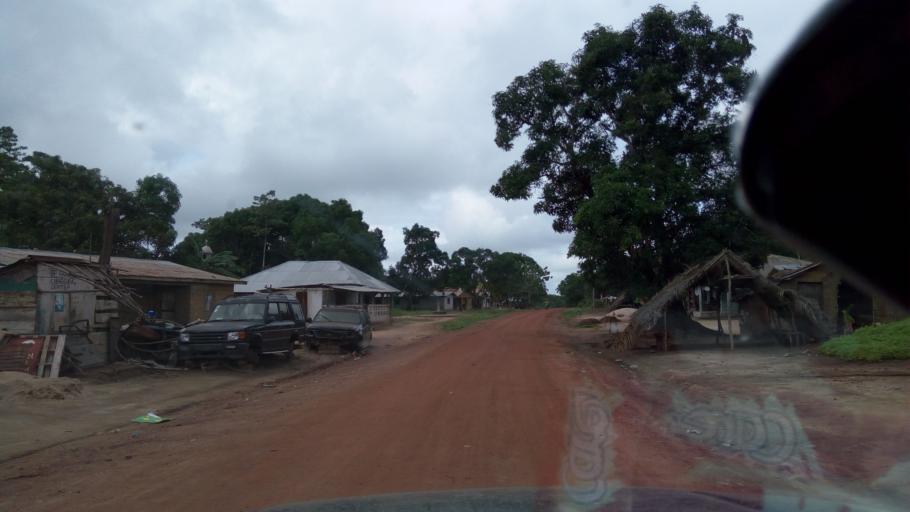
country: SL
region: Northern Province
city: Pepel
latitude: 8.6881
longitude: -12.9982
